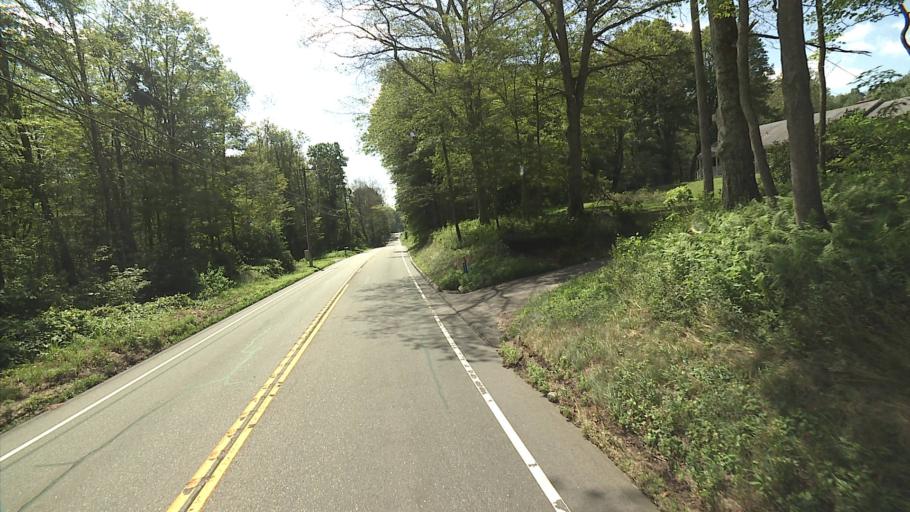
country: US
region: Connecticut
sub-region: Windham County
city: Plainfield Village
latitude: 41.7038
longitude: -72.0085
